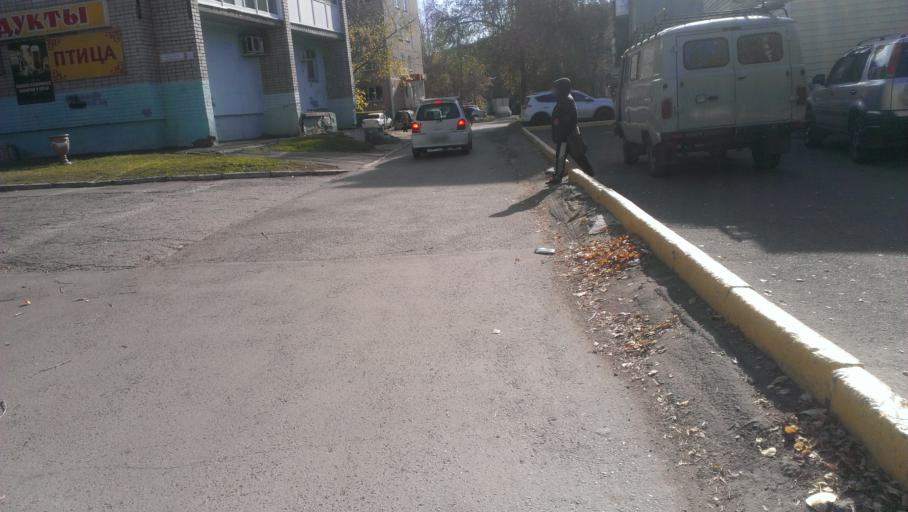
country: RU
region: Altai Krai
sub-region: Gorod Barnaulskiy
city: Barnaul
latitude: 53.3511
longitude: 83.6886
